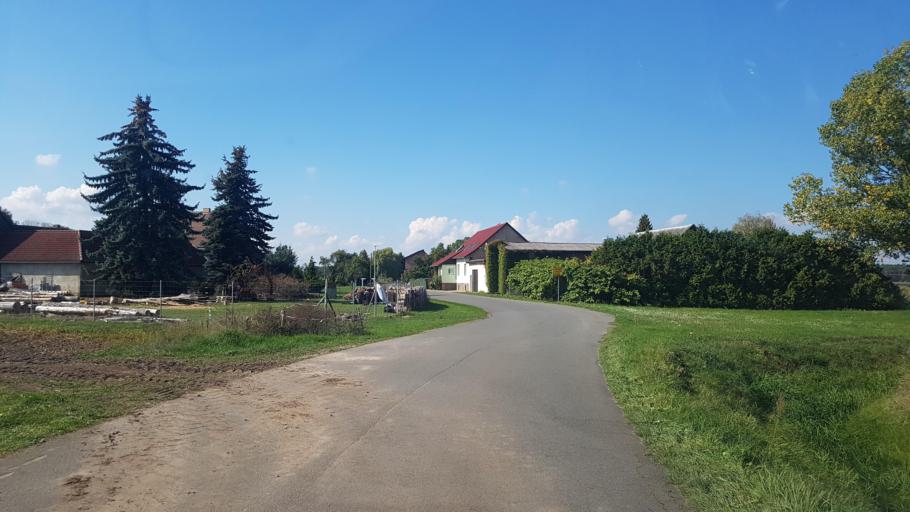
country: DE
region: Brandenburg
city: Ihlow
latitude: 51.8326
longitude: 13.3646
